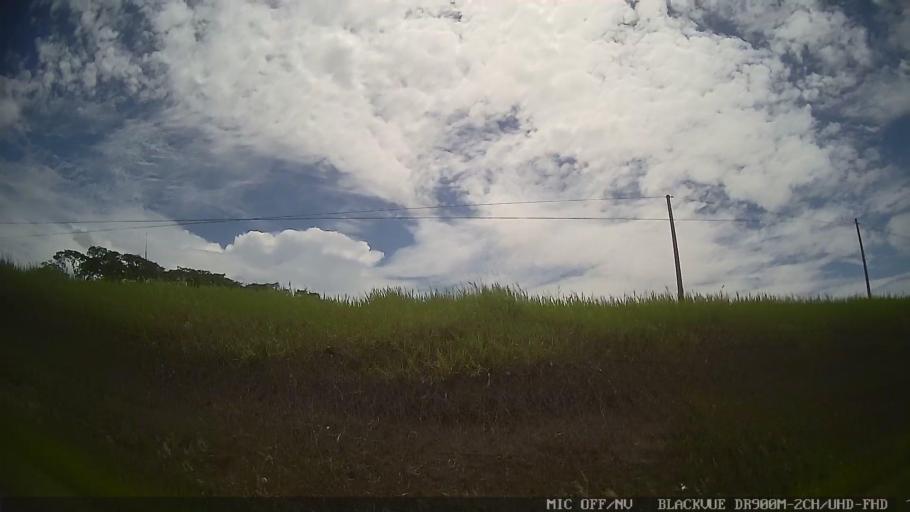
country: BR
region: Sao Paulo
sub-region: Conchas
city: Conchas
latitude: -23.0478
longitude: -47.9589
